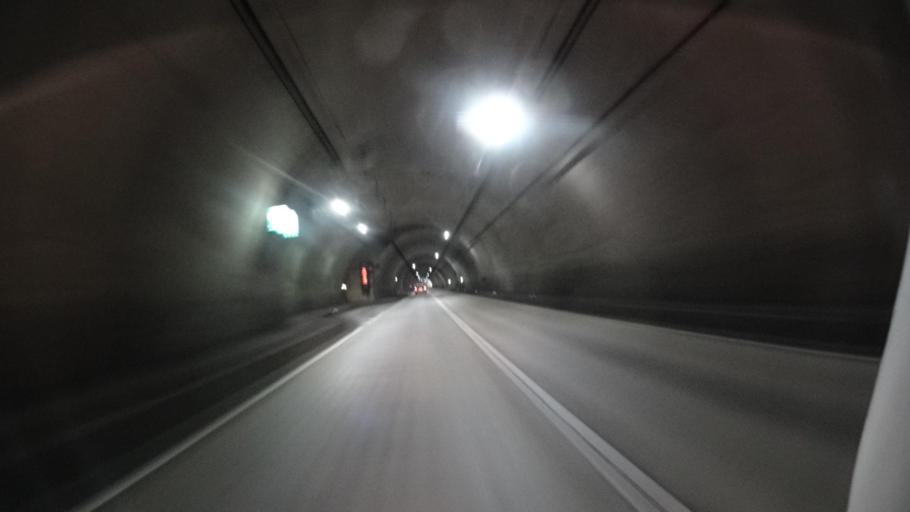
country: JP
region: Kyoto
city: Kameoka
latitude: 35.2259
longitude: 135.5730
